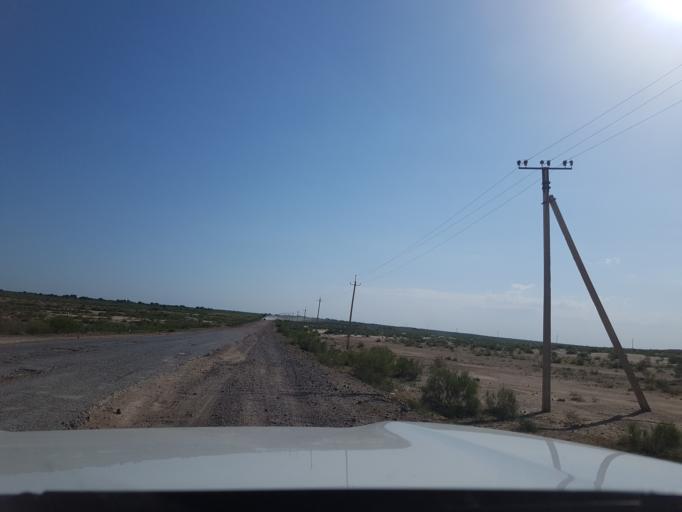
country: TM
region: Dasoguz
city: Koeneuergench
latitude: 42.0296
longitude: 58.8005
